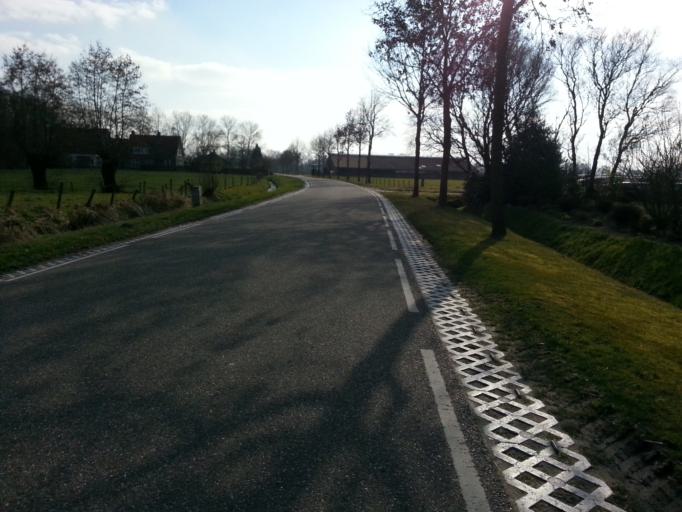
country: NL
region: Utrecht
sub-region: Gemeente Woudenberg
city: Woudenberg
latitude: 52.0971
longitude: 5.4507
